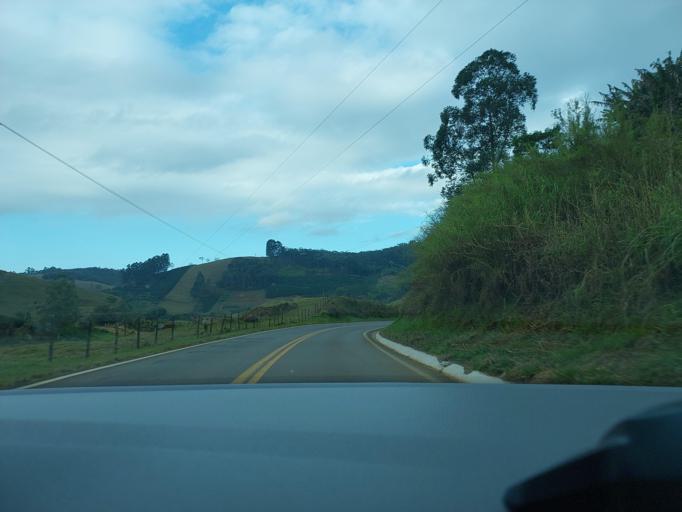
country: BR
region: Minas Gerais
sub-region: Mirai
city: Mirai
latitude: -20.9976
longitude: -42.5506
